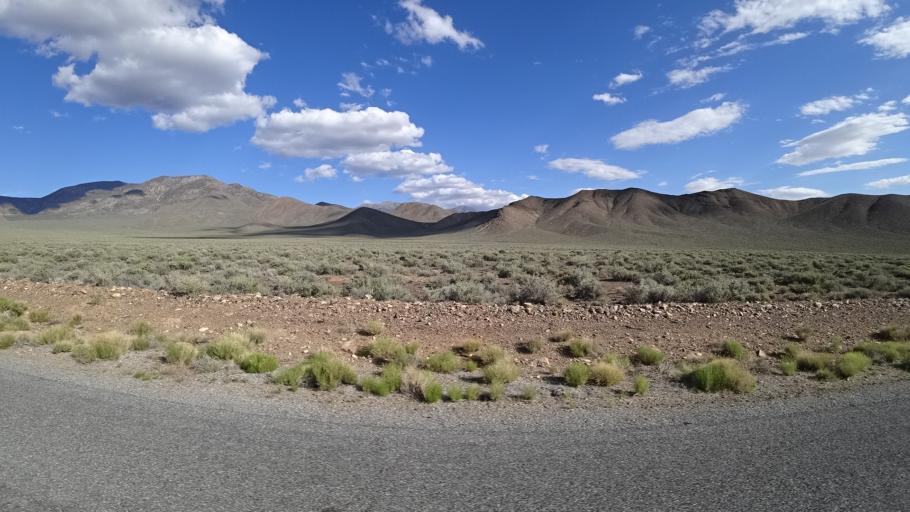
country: US
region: California
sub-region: San Bernardino County
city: Searles Valley
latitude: 36.3047
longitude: -117.1604
